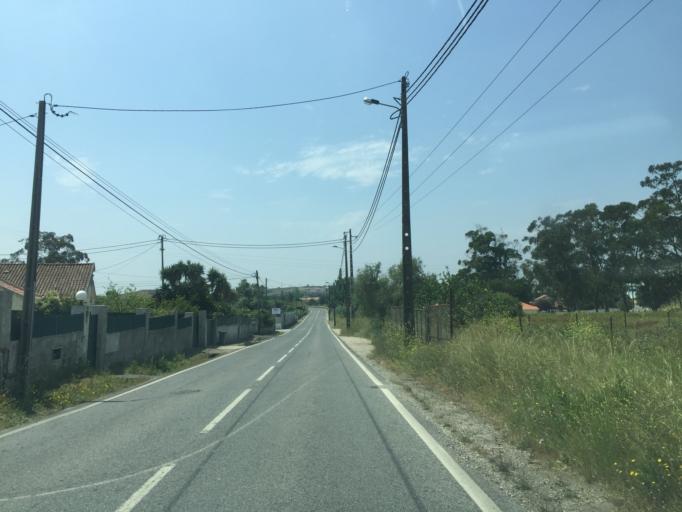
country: PT
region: Lisbon
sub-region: Mafra
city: Venda do Pinheiro
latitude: 38.8926
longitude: -9.1884
